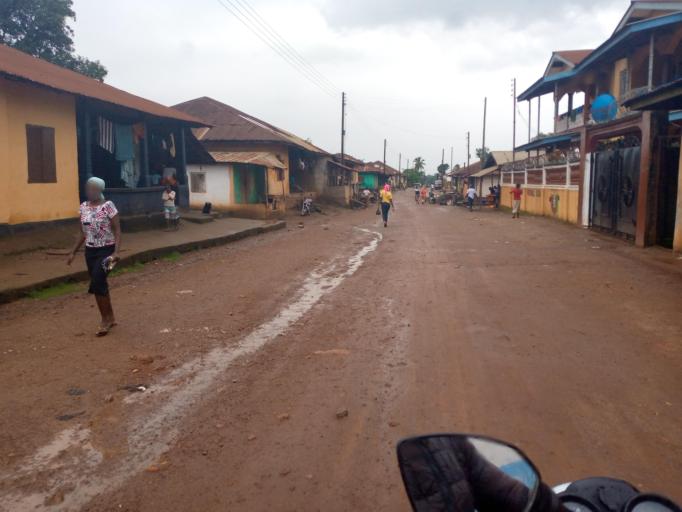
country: SL
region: Eastern Province
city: Kenema
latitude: 7.8799
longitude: -11.1861
